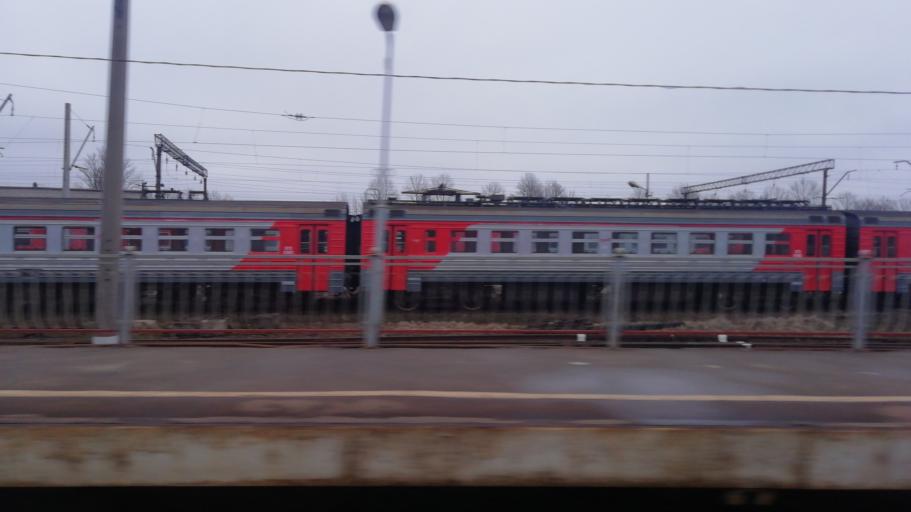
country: RU
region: St.-Petersburg
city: Kupchino
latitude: 59.8888
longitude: 30.3454
